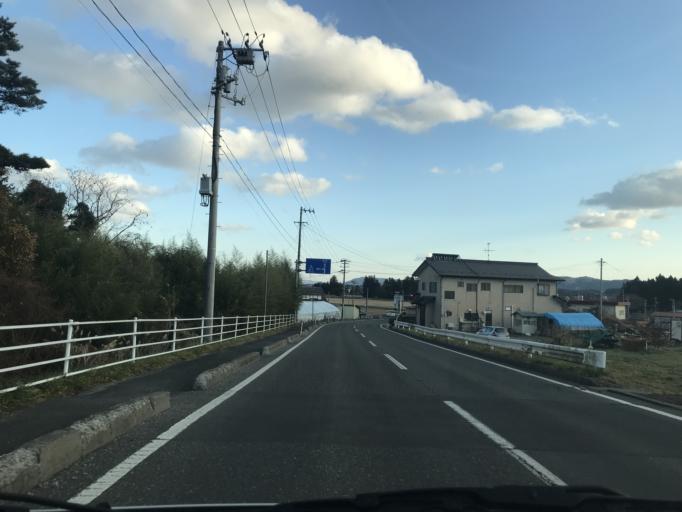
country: JP
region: Miyagi
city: Kogota
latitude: 38.6511
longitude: 141.0745
